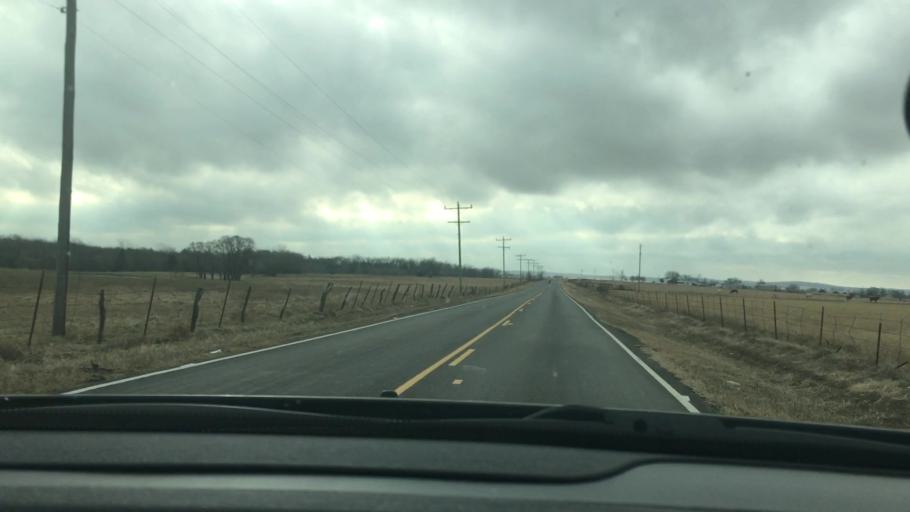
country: US
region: Oklahoma
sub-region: Bryan County
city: Durant
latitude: 34.1268
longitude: -96.4903
